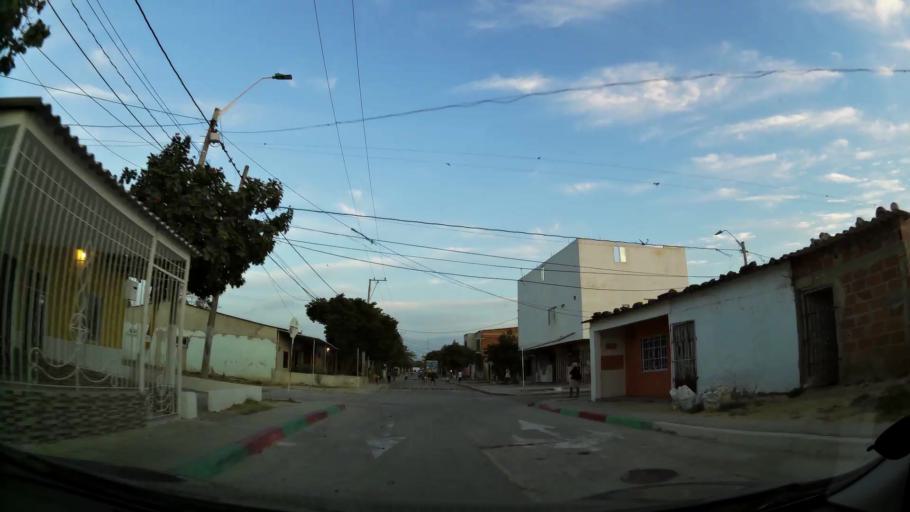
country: CO
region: Atlantico
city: Barranquilla
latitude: 10.9600
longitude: -74.8218
